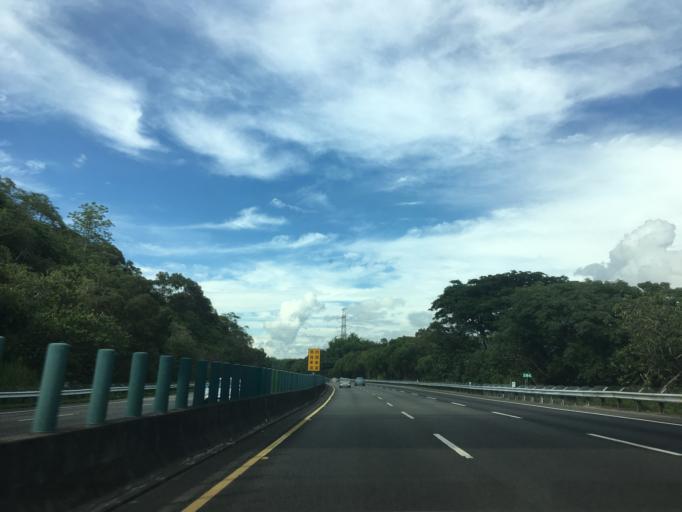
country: TW
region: Taiwan
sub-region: Chiayi
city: Jiayi Shi
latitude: 23.5415
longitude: 120.4992
